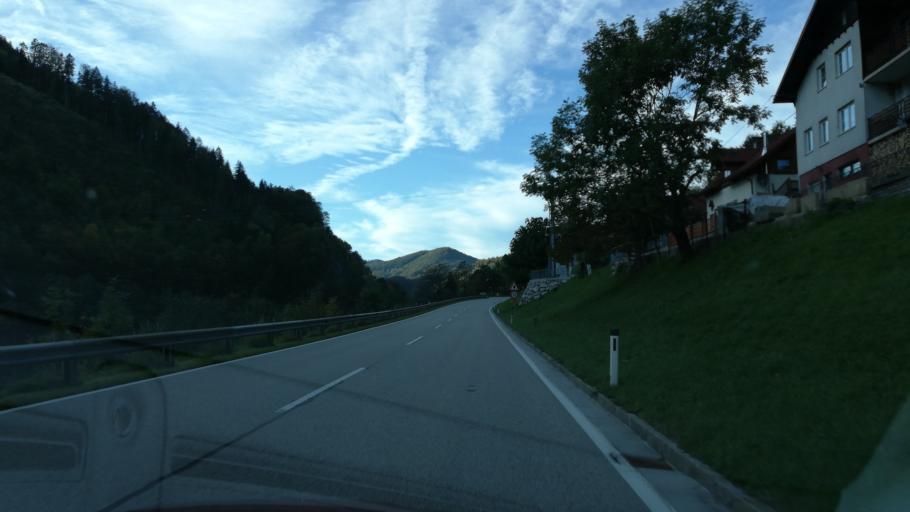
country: AT
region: Upper Austria
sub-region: Politischer Bezirk Steyr-Land
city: Losenstein
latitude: 47.9145
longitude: 14.4471
